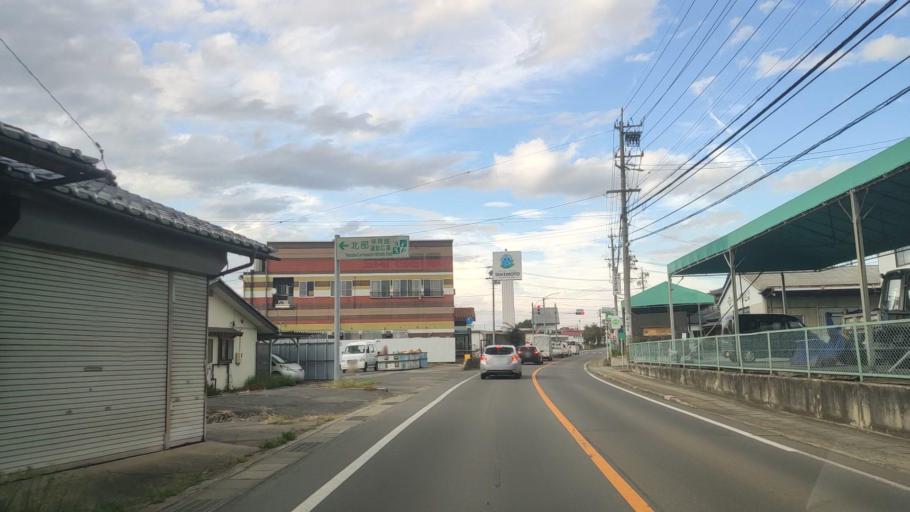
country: JP
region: Nagano
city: Suzaka
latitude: 36.6706
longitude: 138.3158
